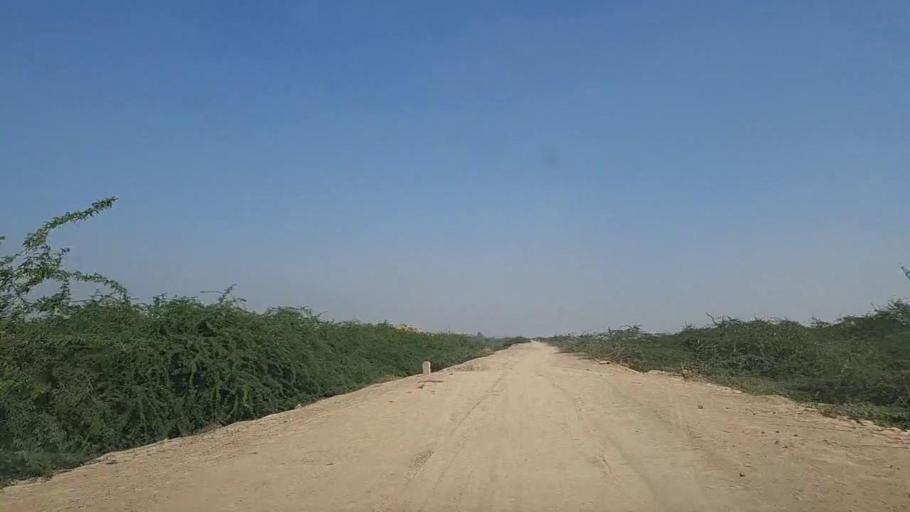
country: PK
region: Sindh
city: Daro Mehar
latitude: 24.8645
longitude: 68.0422
